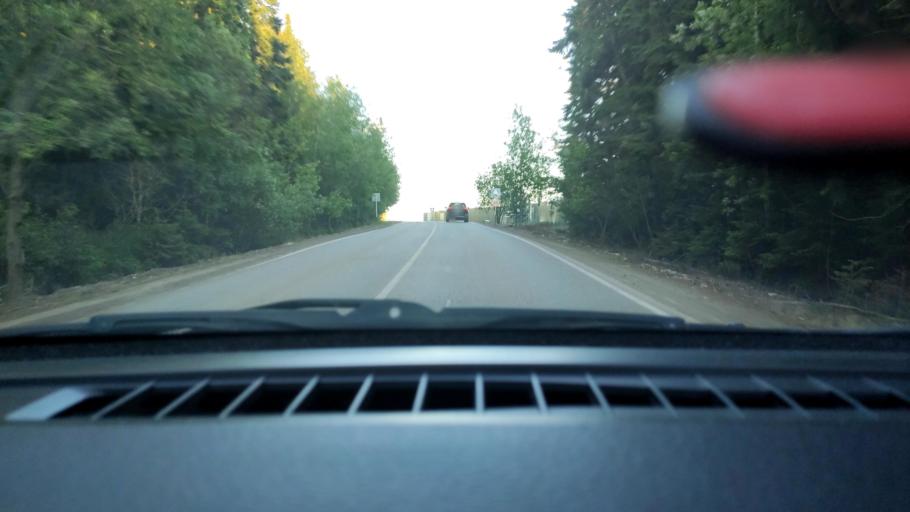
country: RU
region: Perm
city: Kultayevo
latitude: 57.9197
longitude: 55.9284
